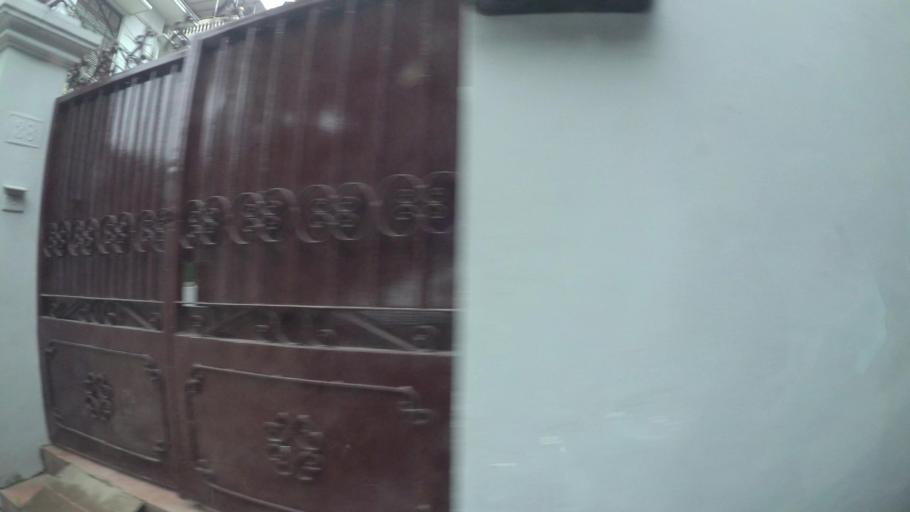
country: VN
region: Ha Noi
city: Tay Ho
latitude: 21.0571
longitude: 105.8329
